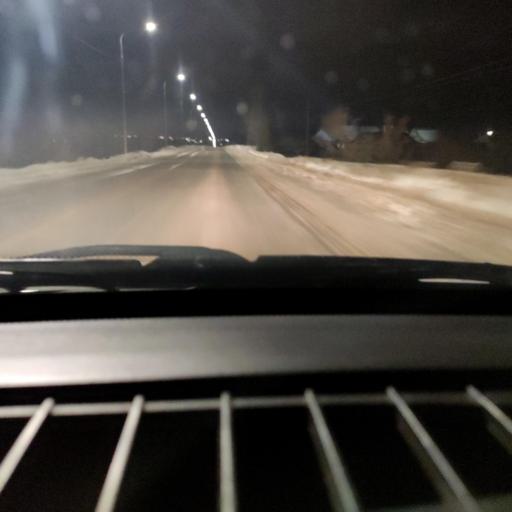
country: RU
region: Bashkortostan
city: Kabakovo
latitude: 54.5798
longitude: 56.2866
